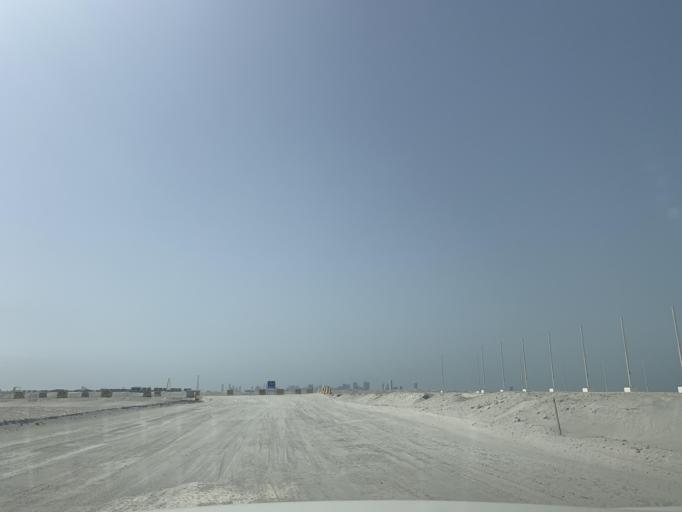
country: BH
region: Northern
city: Sitrah
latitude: 26.1605
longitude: 50.6419
